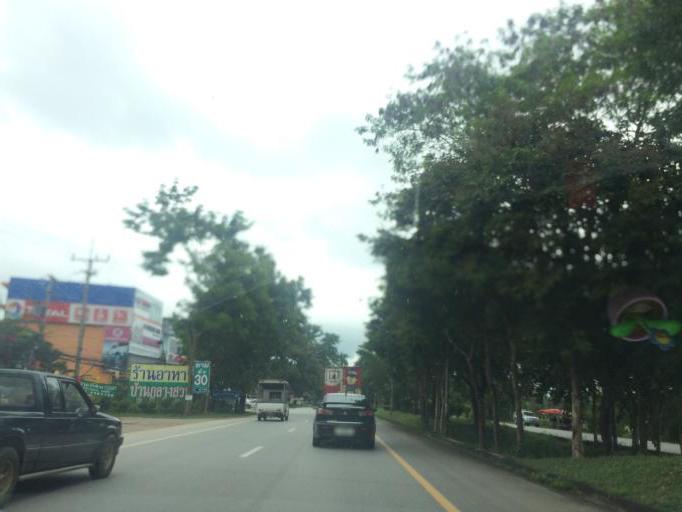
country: TH
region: Chiang Rai
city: Chiang Rai
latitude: 19.8686
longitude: 99.8247
